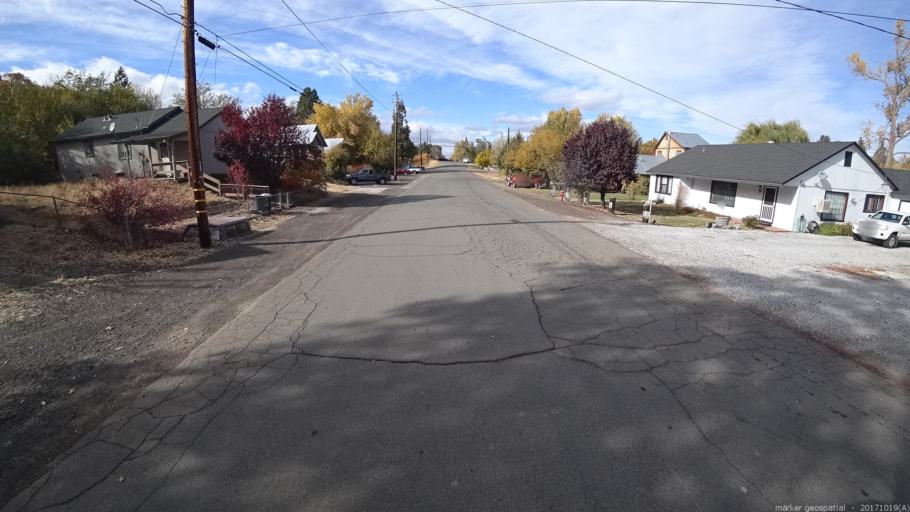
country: US
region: California
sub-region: Shasta County
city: Burney
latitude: 41.0014
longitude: -121.4420
